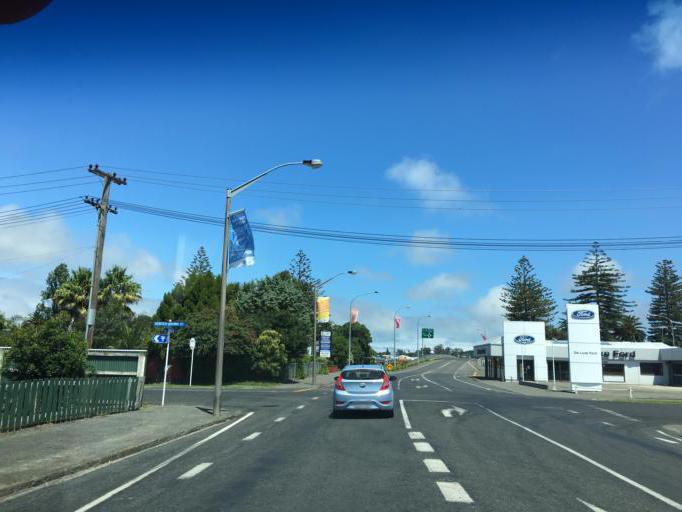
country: NZ
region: Hawke's Bay
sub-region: Wairoa District
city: Wairoa
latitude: -39.0294
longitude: 177.4191
